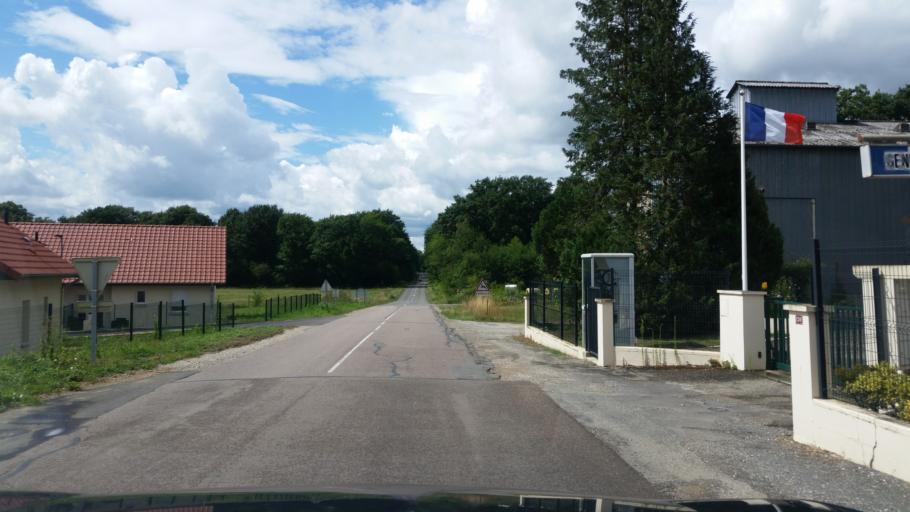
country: FR
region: Franche-Comte
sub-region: Departement du Jura
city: Bletterans
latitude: 46.6727
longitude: 5.3914
